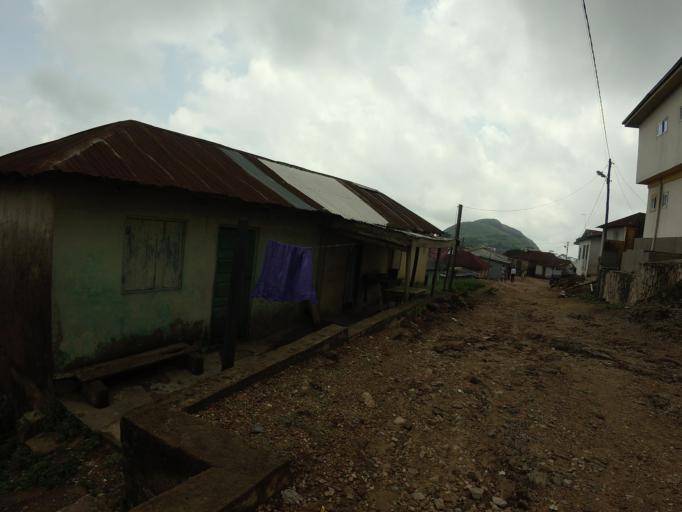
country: TG
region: Plateaux
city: Kpalime
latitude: 6.8464
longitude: 0.4362
